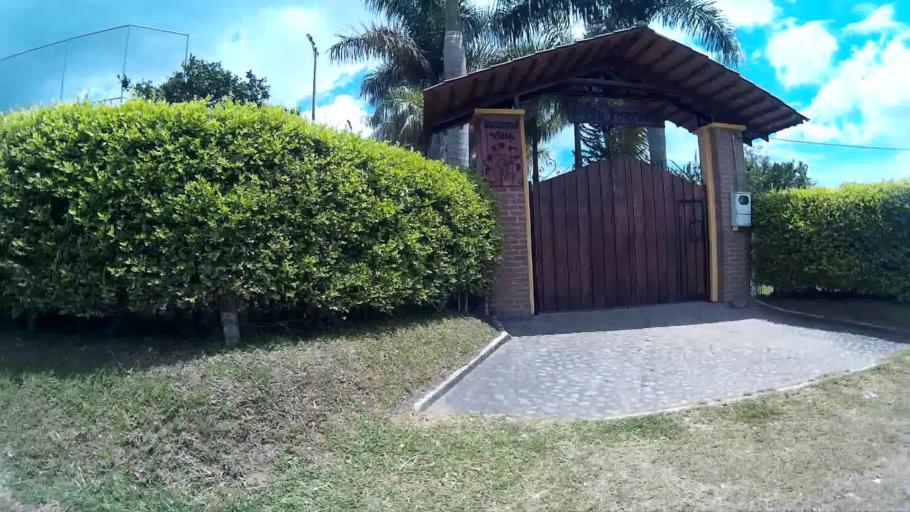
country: CO
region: Quindio
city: Filandia
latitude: 4.7205
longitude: -75.6842
